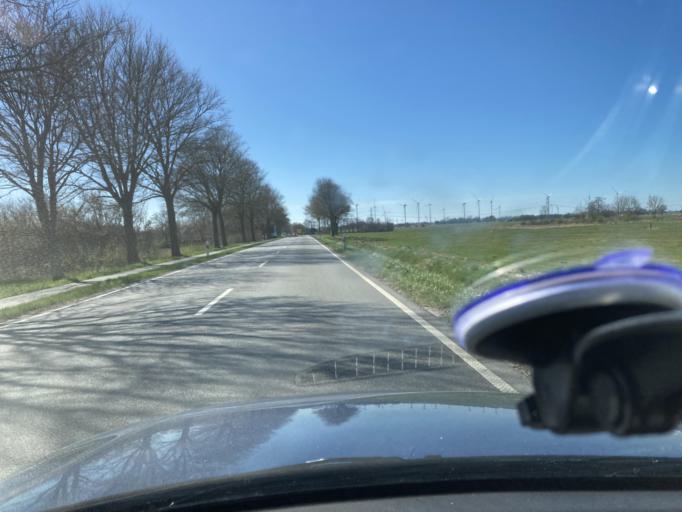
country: DE
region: Schleswig-Holstein
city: Lohe-Rickelshof
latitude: 54.1925
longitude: 9.0669
